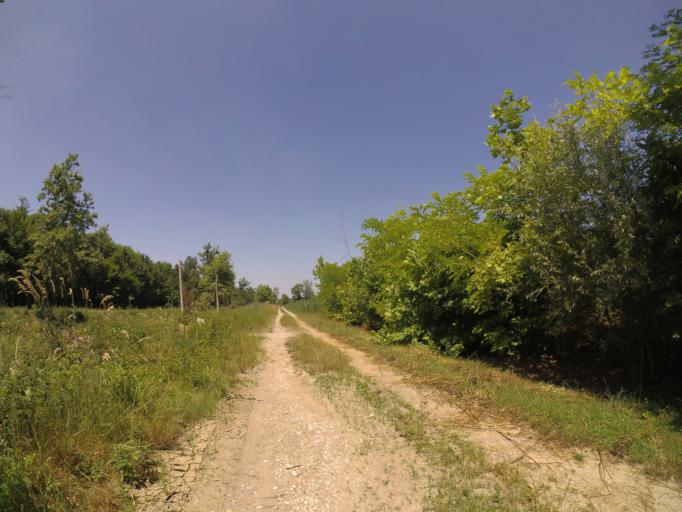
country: IT
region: Friuli Venezia Giulia
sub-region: Provincia di Udine
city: Rivignano
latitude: 45.9065
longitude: 13.0283
